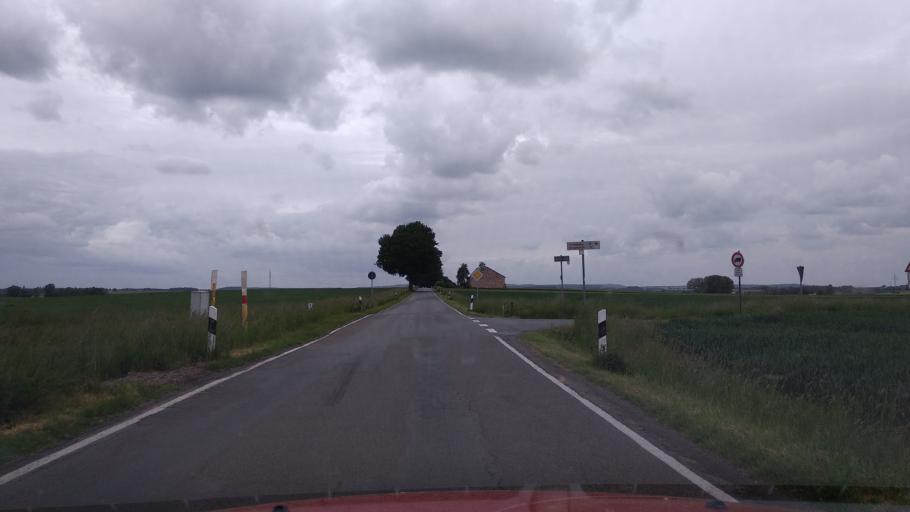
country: DE
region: North Rhine-Westphalia
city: Borgentreich
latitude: 51.5447
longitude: 9.1986
